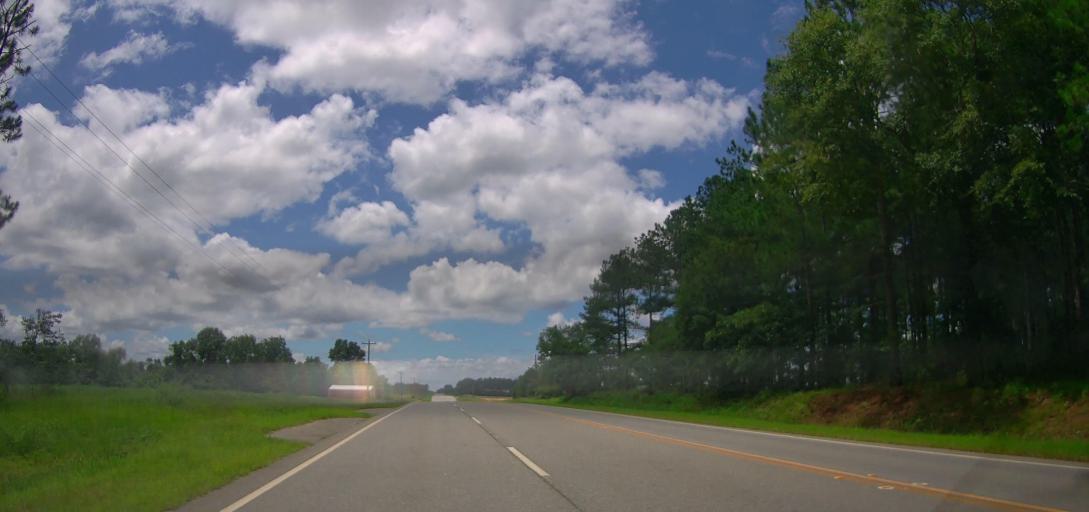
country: US
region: Georgia
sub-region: Turner County
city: Ashburn
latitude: 31.7218
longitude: -83.5266
